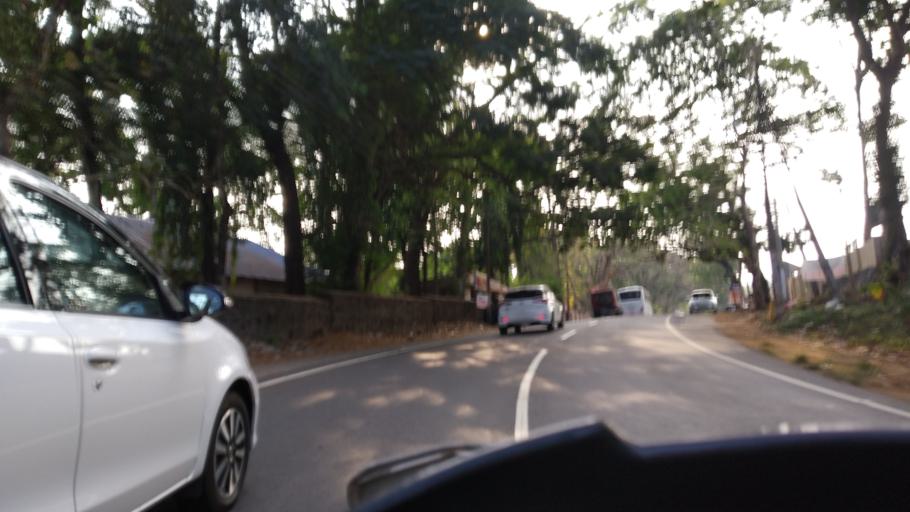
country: IN
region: Kerala
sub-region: Kottayam
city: Erattupetta
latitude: 9.5697
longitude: 76.8186
